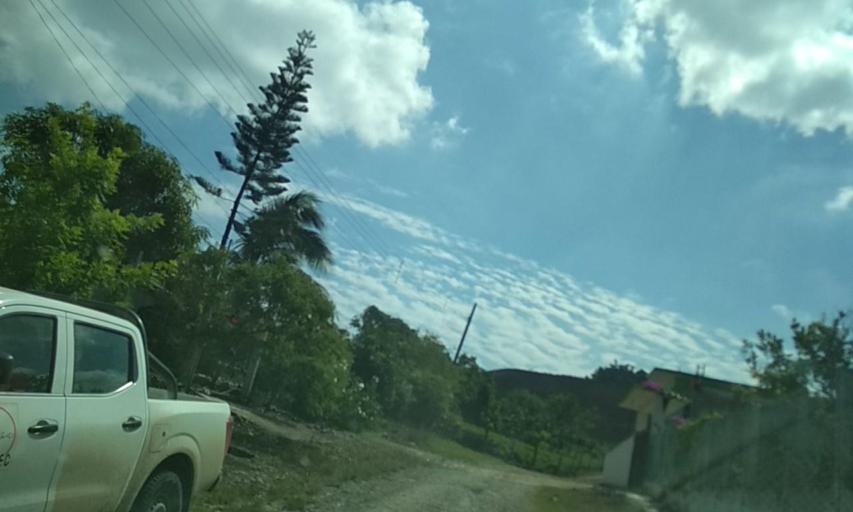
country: MX
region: Veracruz
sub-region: Cazones de Herrera
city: Rancho Nuevo
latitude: 20.6401
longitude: -97.2483
